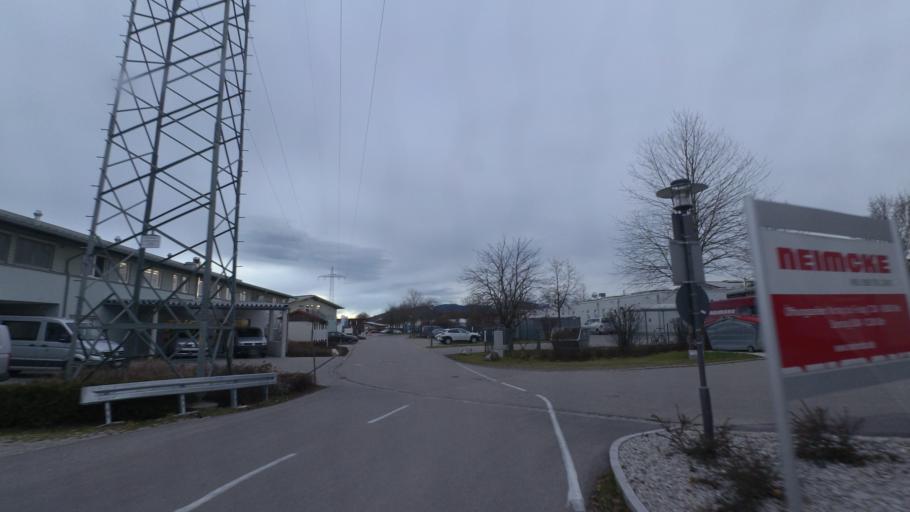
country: DE
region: Bavaria
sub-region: Upper Bavaria
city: Vachendorf
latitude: 47.8710
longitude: 12.6150
